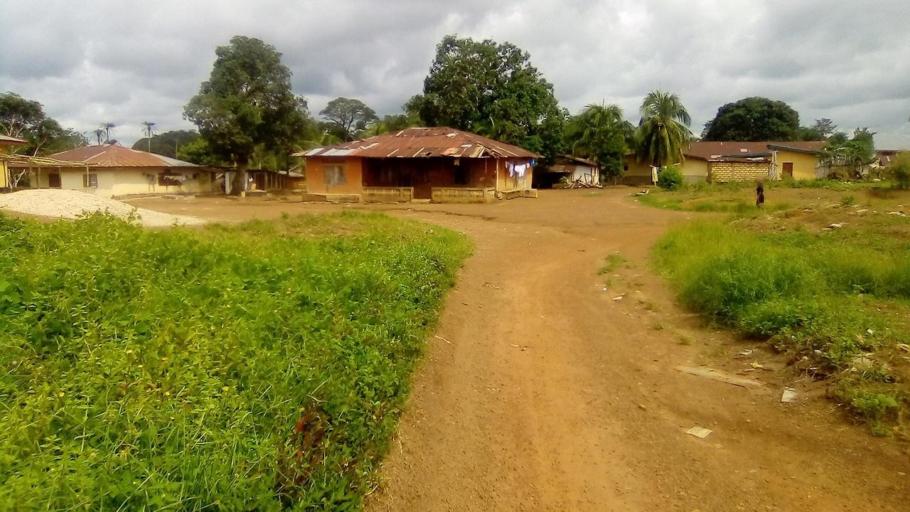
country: SL
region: Southern Province
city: Pujehun
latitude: 7.3609
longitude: -11.7251
